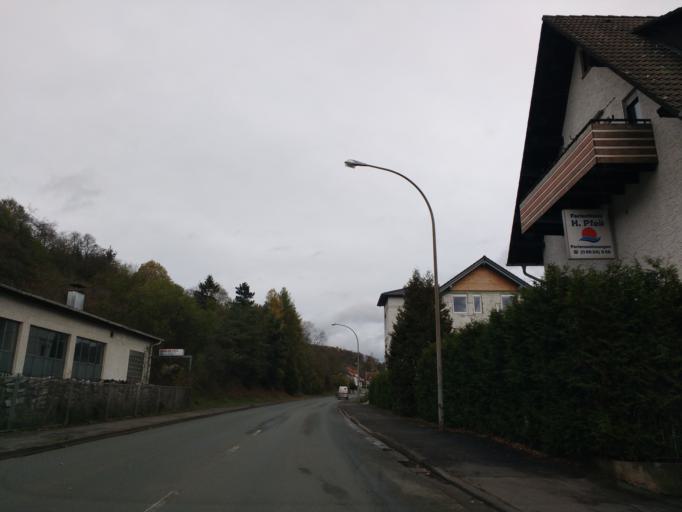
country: DE
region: Hesse
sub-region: Regierungsbezirk Kassel
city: Sachsenhausen
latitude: 51.2116
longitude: 9.0090
